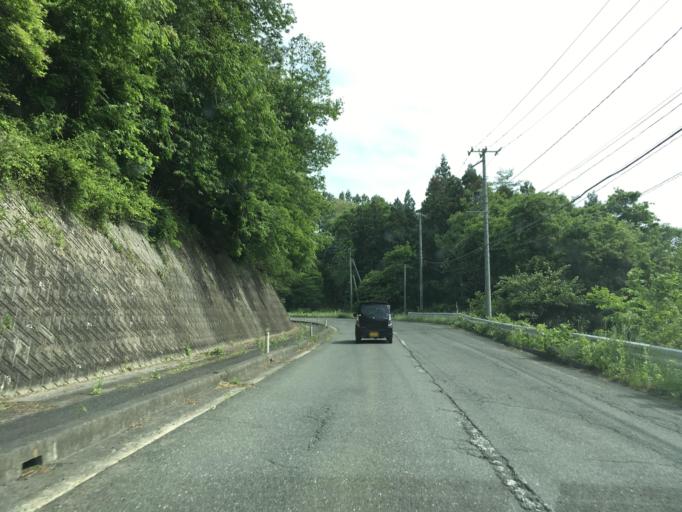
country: JP
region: Iwate
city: Mizusawa
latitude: 39.0665
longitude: 141.3568
